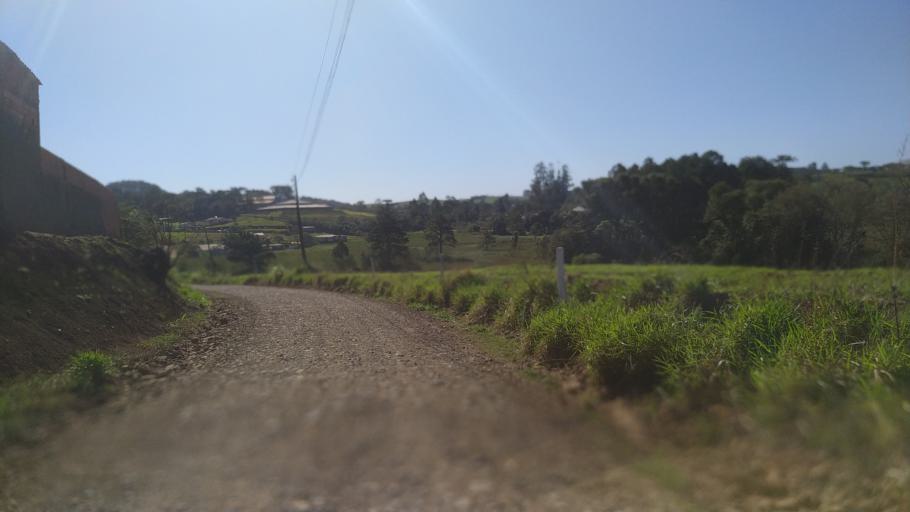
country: BR
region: Santa Catarina
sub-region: Chapeco
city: Chapeco
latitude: -27.1495
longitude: -52.5956
